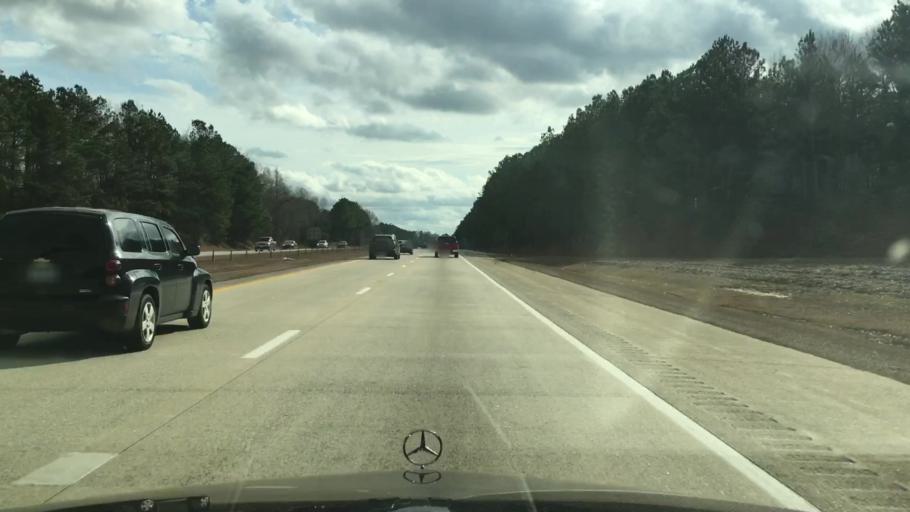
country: US
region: North Carolina
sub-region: Johnston County
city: Benson
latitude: 35.4213
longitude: -78.5296
